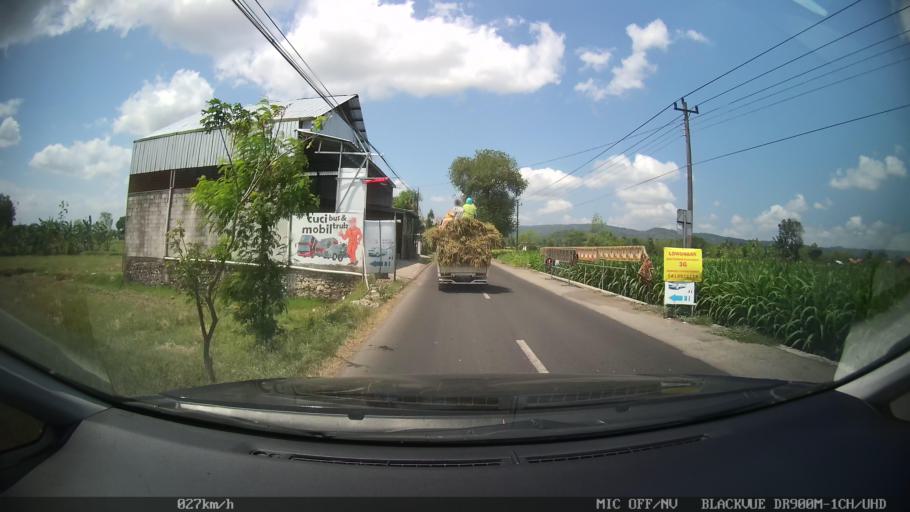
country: ID
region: Daerah Istimewa Yogyakarta
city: Sewon
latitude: -7.8976
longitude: 110.3761
